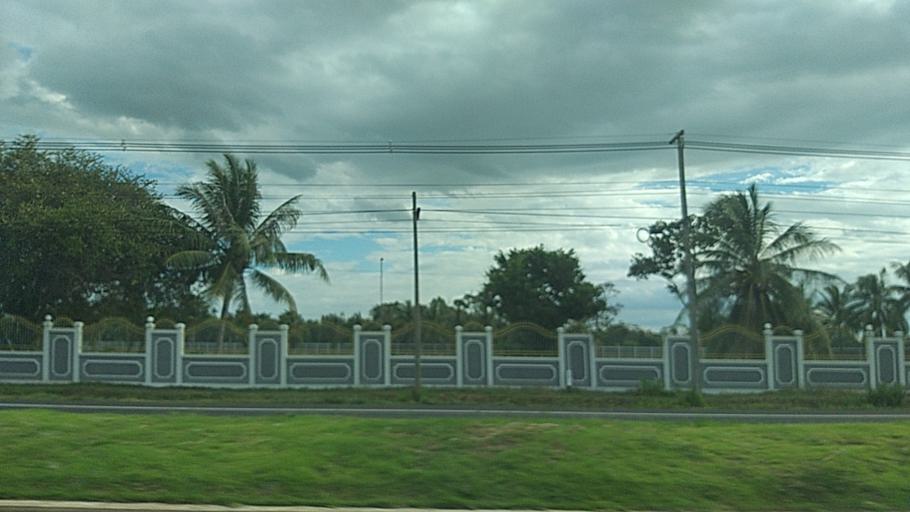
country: TH
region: Surin
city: Prasat
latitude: 14.5976
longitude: 103.4391
